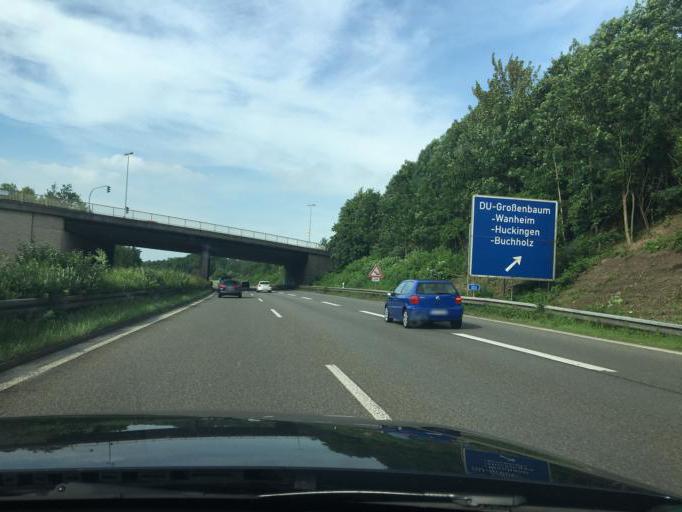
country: DE
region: North Rhine-Westphalia
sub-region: Regierungsbezirk Dusseldorf
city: Hochfeld
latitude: 51.3700
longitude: 6.7728
